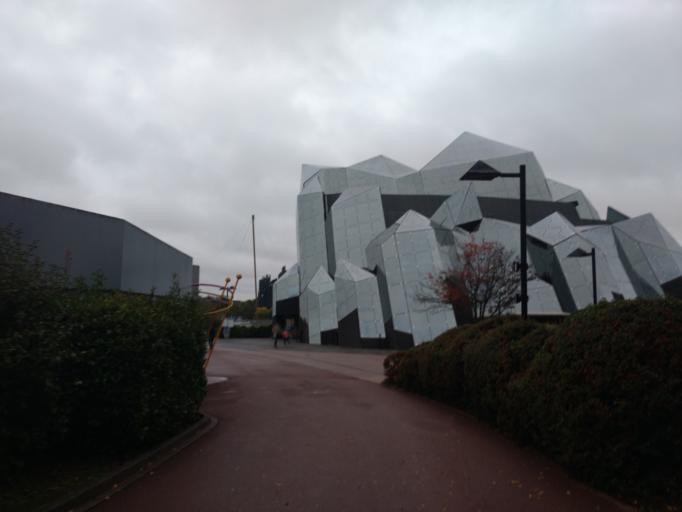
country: FR
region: Poitou-Charentes
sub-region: Departement de la Vienne
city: Jaunay-Clan
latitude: 46.6704
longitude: 0.3703
